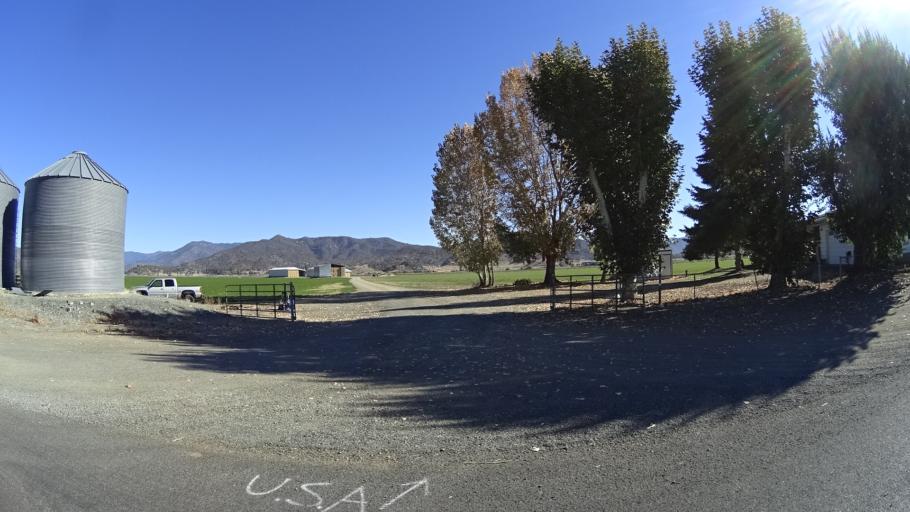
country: US
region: California
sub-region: Siskiyou County
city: Yreka
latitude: 41.5748
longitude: -122.8556
